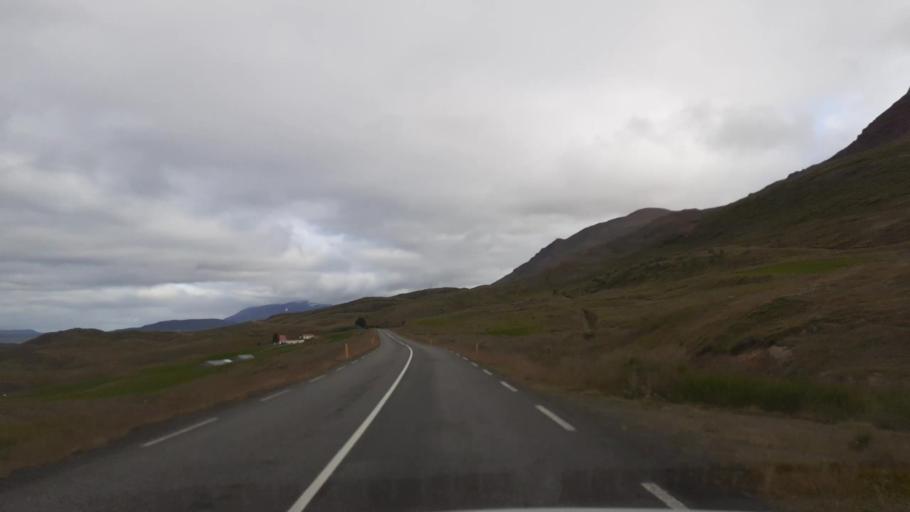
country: IS
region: Northeast
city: Akureyri
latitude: 65.8165
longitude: -18.0483
